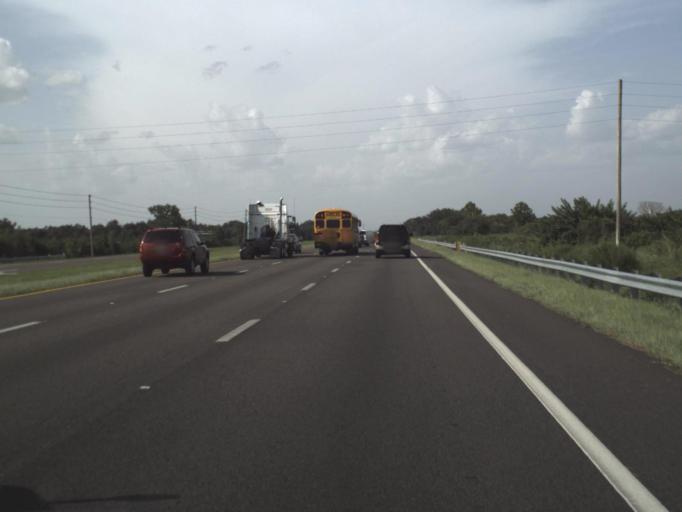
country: US
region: Florida
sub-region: Polk County
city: Dundee
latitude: 27.9926
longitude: -81.6310
